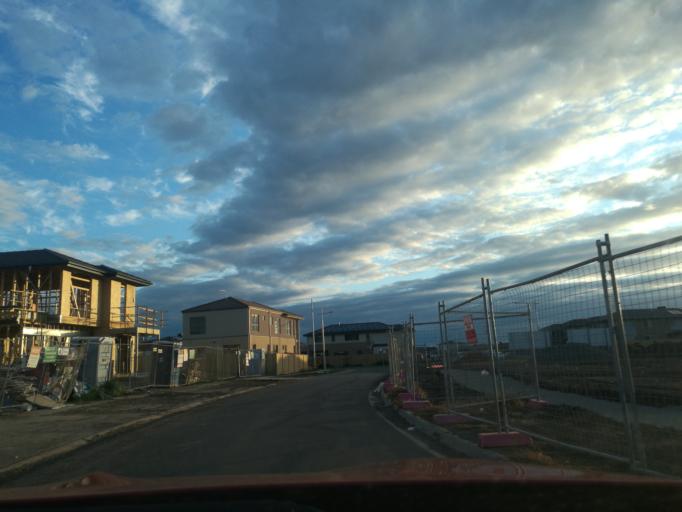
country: AU
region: Victoria
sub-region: Hobsons Bay
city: Altona Meadows
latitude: -37.9136
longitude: 144.7860
